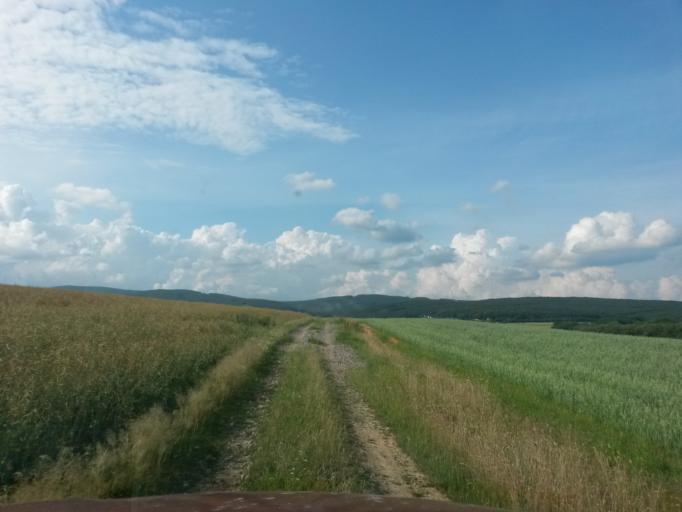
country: SK
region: Kosicky
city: Moldava nad Bodvou
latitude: 48.6606
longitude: 21.1117
